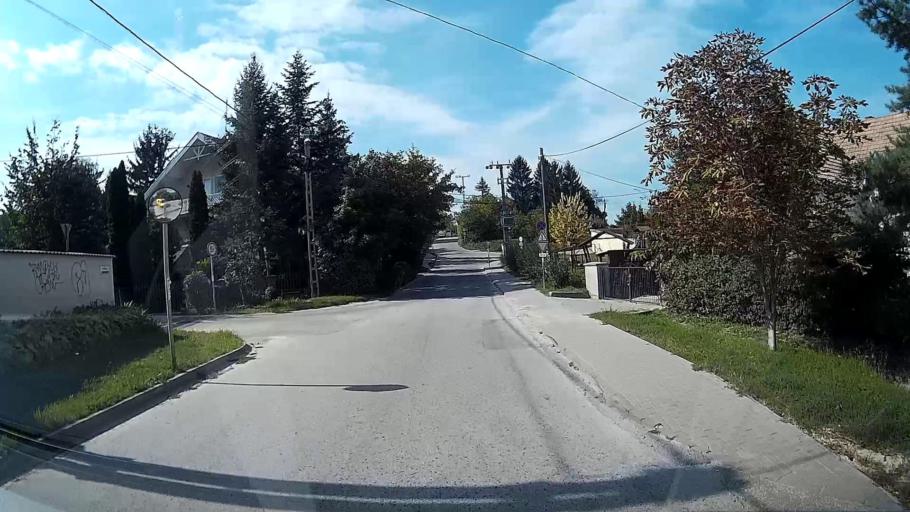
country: HU
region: Pest
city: Solymar
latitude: 47.5920
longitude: 18.9205
